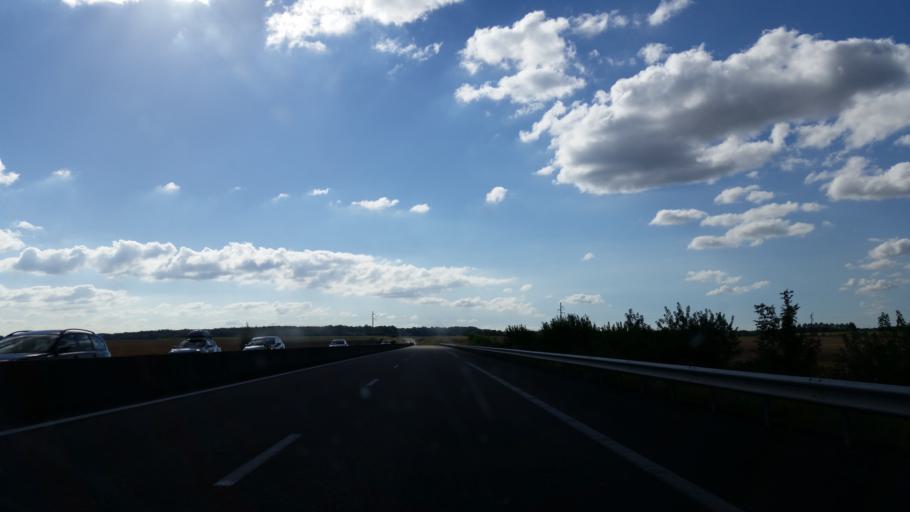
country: FR
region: Picardie
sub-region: Departement de la Somme
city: Hornoy-le-Bourg
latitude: 49.8141
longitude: 1.9335
